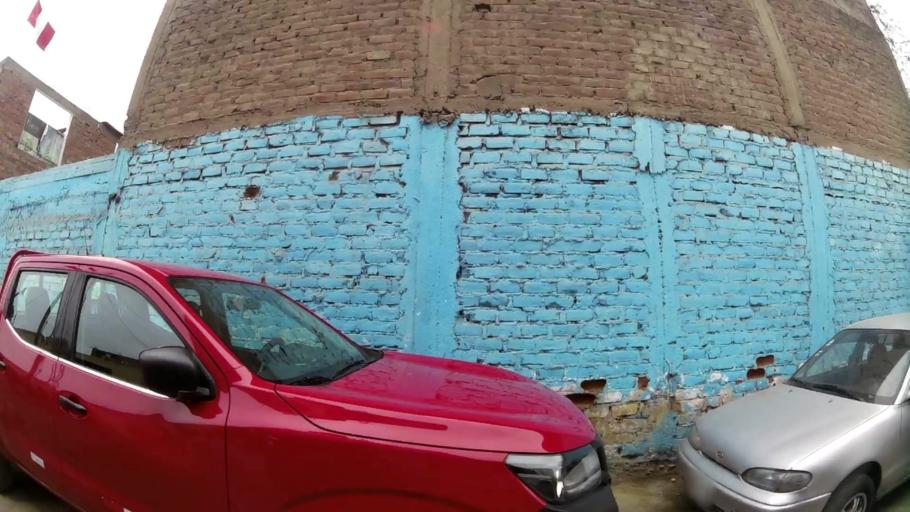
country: PE
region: Lima
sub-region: Lima
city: Surco
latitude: -12.1461
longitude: -77.0096
